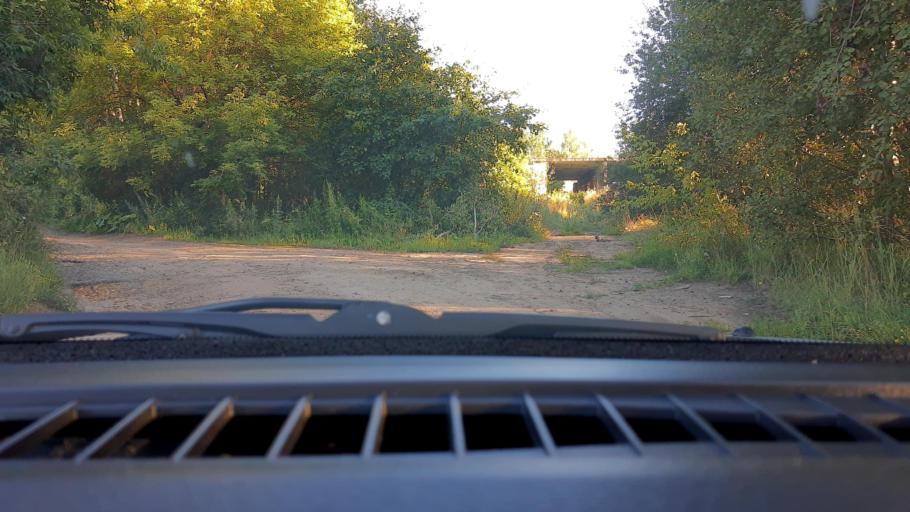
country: RU
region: Nizjnij Novgorod
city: Afonino
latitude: 56.1305
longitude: 44.0615
